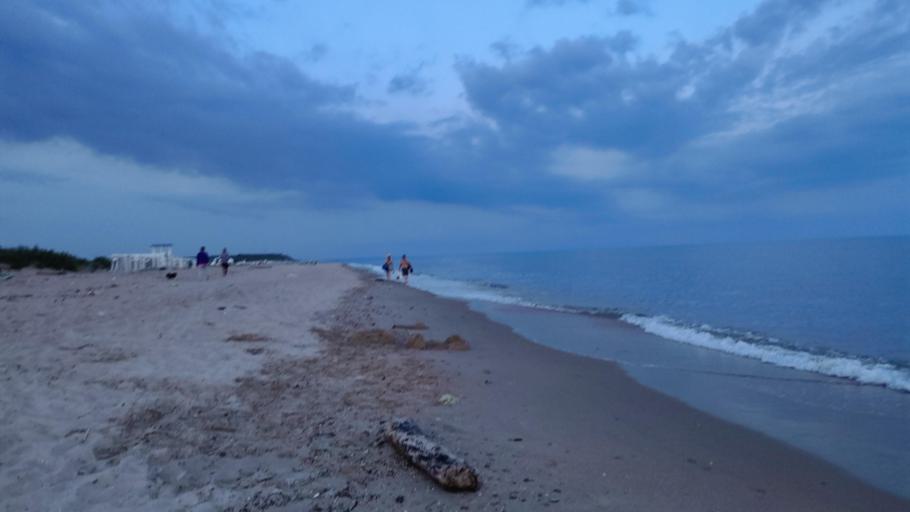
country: RU
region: Krasnodarskiy
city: Blagovetschenskaya
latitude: 45.0672
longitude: 37.0299
